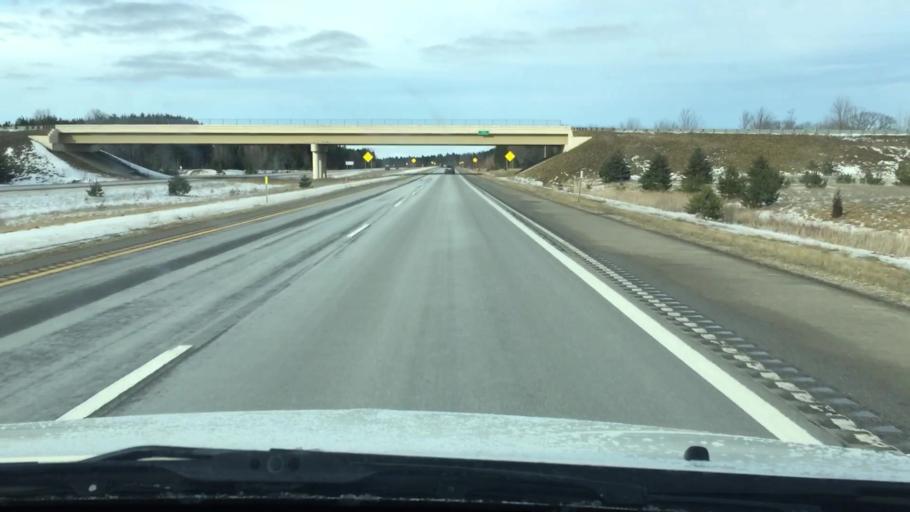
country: US
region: Michigan
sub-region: Wexford County
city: Manton
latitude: 44.4529
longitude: -85.3950
